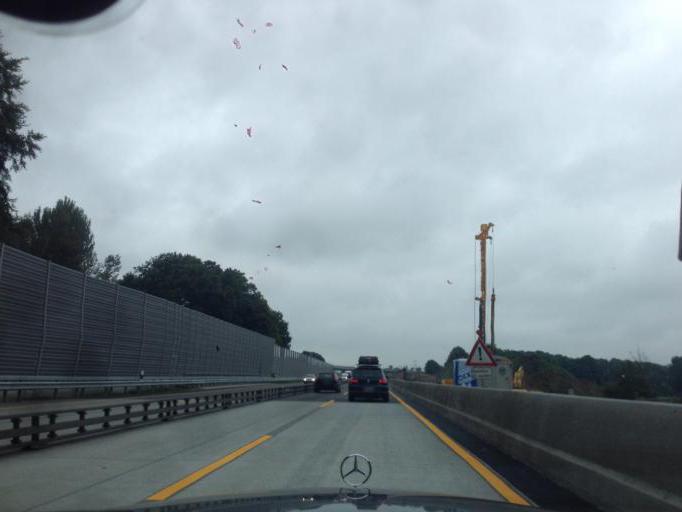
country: DE
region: Schleswig-Holstein
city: Bimohlen
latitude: 53.9348
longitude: 9.9446
